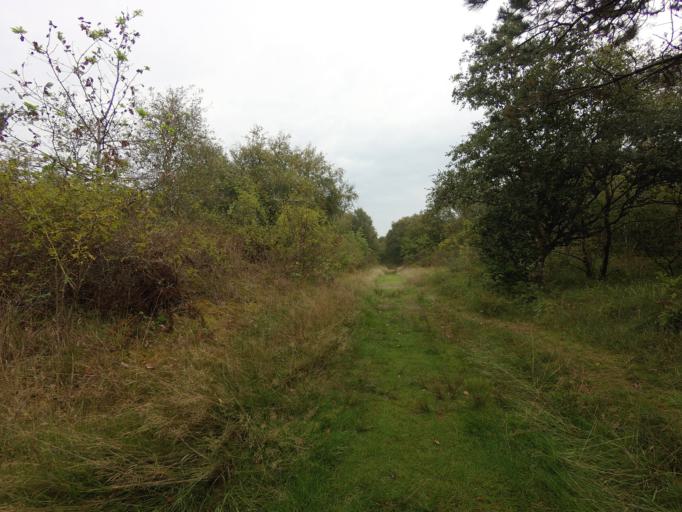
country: NL
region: Friesland
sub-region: Gemeente Schiermonnikoog
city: Schiermonnikoog
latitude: 53.4869
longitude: 6.1691
